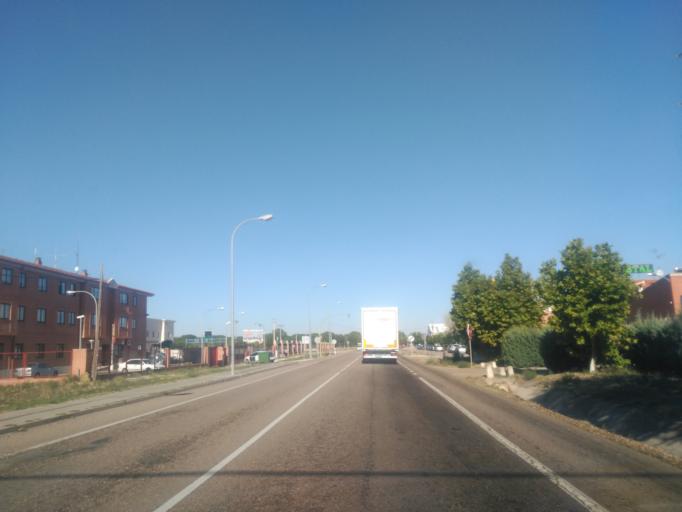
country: ES
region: Castille and Leon
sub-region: Provincia de Valladolid
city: Penafiel
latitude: 41.6007
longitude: -4.1329
